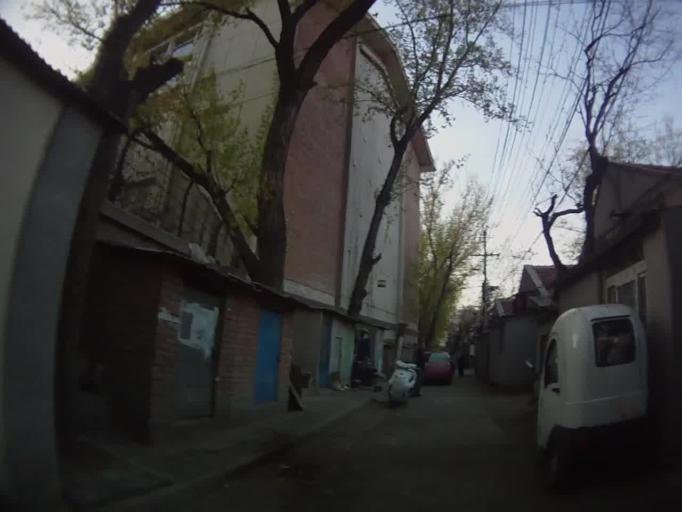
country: CN
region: Beijing
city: Longtan
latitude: 39.8804
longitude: 116.4252
